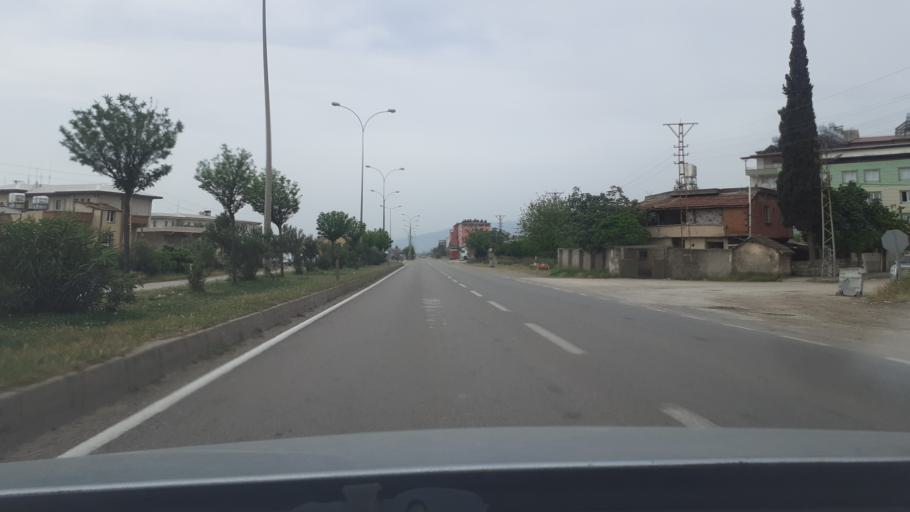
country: TR
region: Hatay
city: Kirikhan
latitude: 36.4852
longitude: 36.3631
